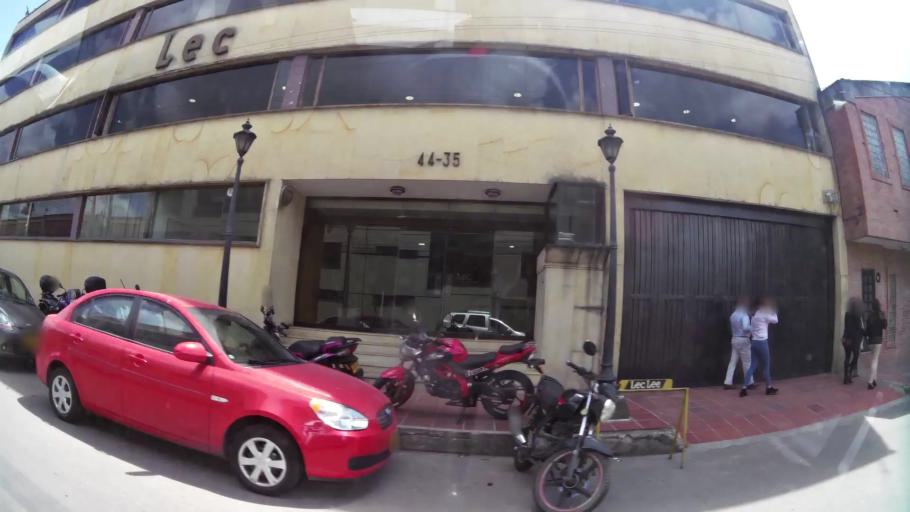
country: CO
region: Bogota D.C.
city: Bogota
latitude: 4.6291
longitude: -74.1006
